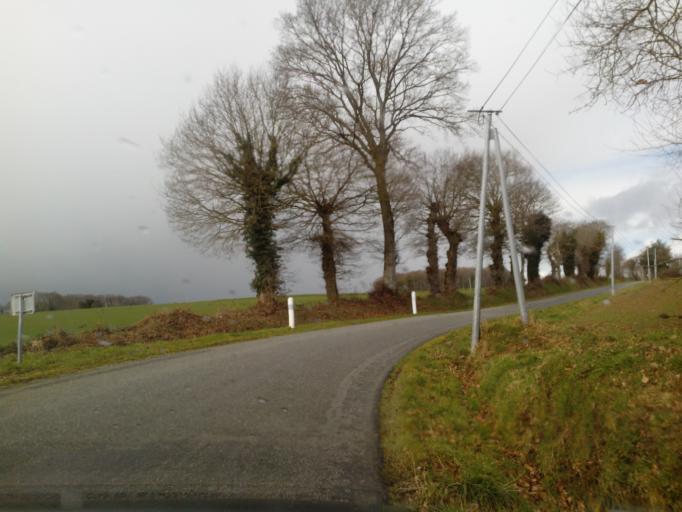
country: FR
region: Brittany
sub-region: Departement des Cotes-d'Armor
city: Merdrignac
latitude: 48.1582
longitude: -2.4197
